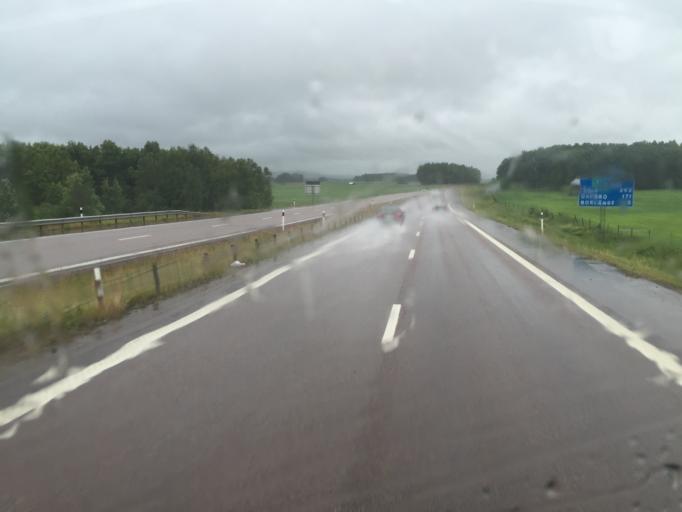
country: SE
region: Dalarna
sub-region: Borlange Kommun
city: Ornas
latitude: 60.4997
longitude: 15.5142
